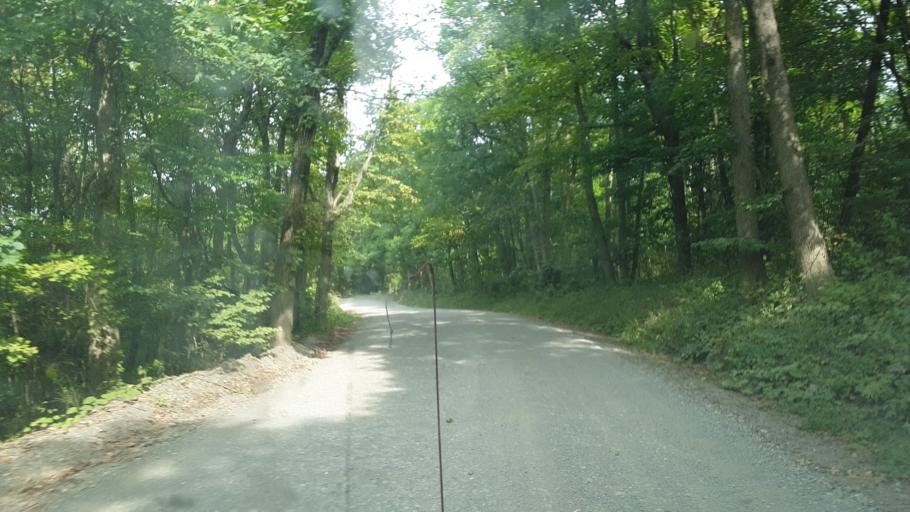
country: US
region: Pennsylvania
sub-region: Jefferson County
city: Punxsutawney
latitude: 40.9327
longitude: -79.0549
